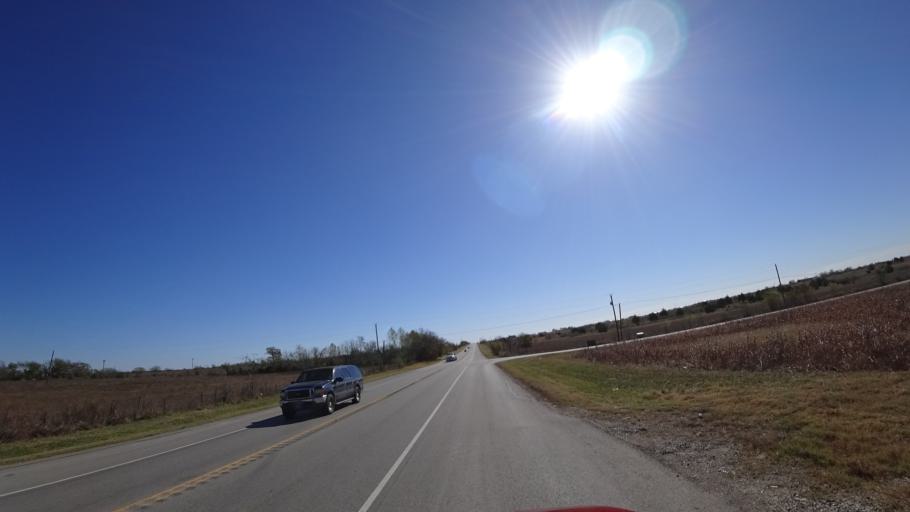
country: US
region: Texas
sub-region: Travis County
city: Garfield
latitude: 30.1106
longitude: -97.6235
